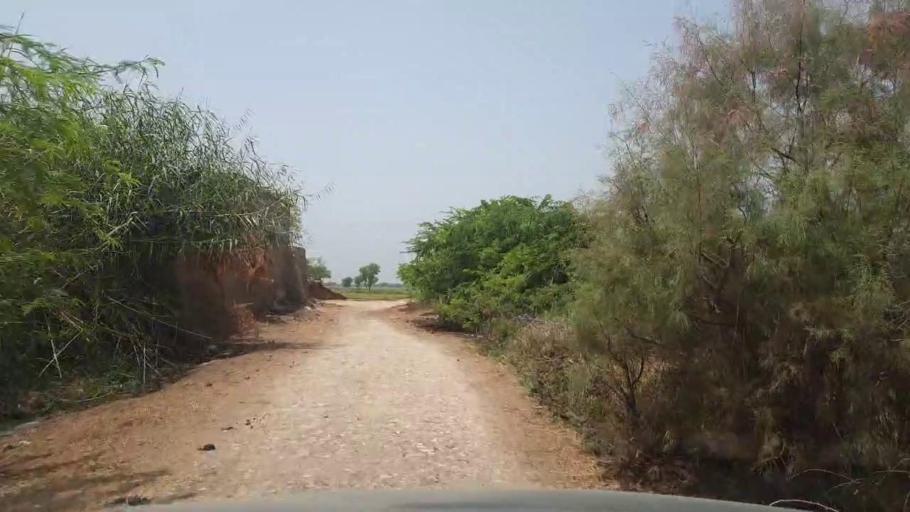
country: PK
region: Sindh
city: Garhi Yasin
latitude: 27.9222
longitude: 68.3718
